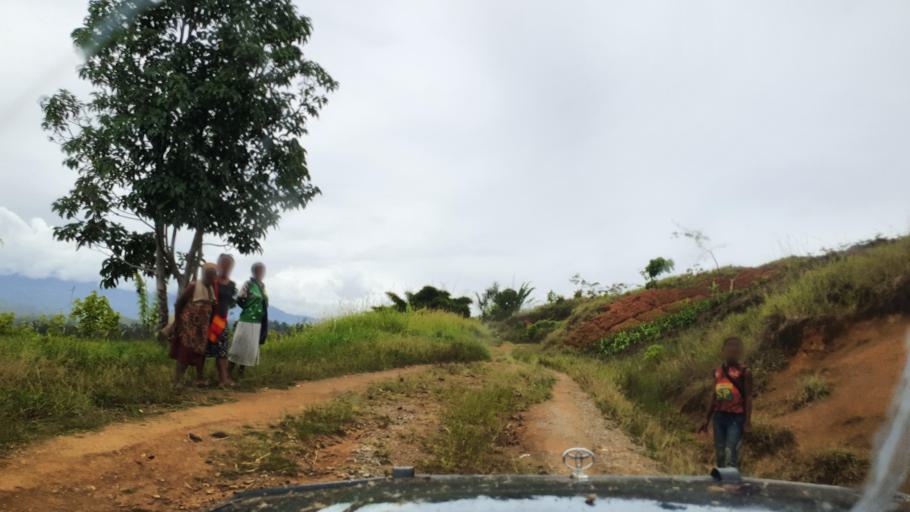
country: PG
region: Jiwaka
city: Minj
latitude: -5.9498
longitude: 144.7705
